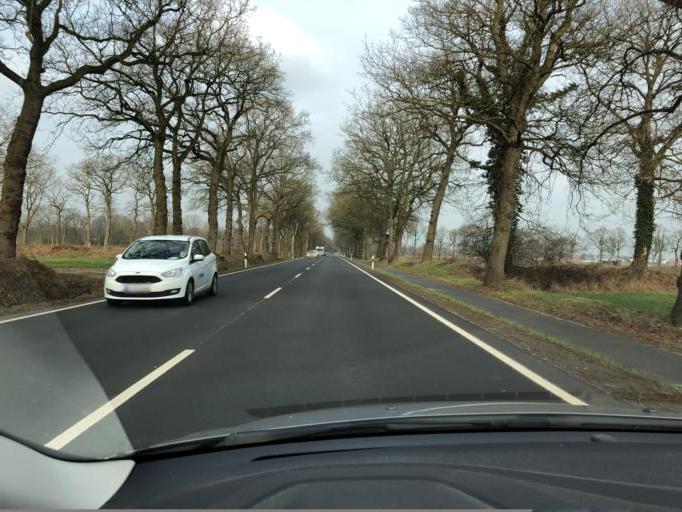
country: DE
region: Lower Saxony
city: Mittegrossefehn
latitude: 53.3651
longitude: 7.5917
